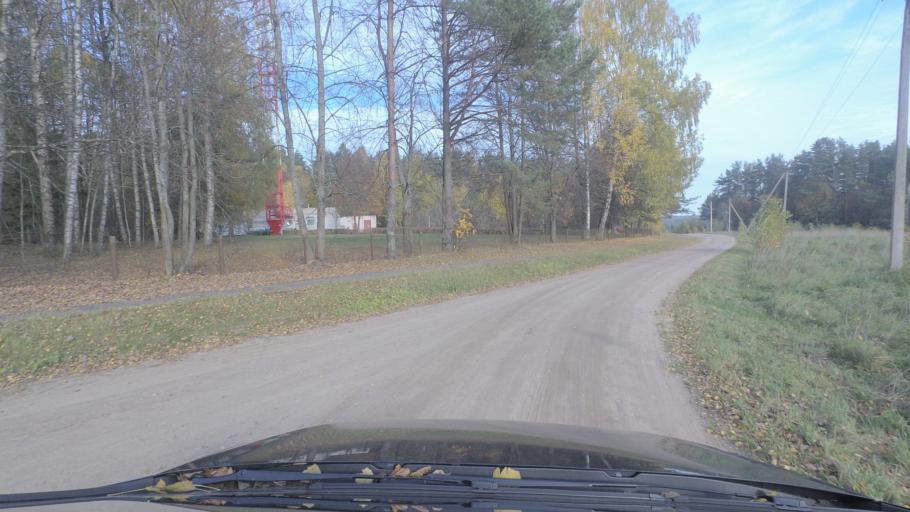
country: LT
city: Ignalina
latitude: 55.3372
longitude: 26.1765
